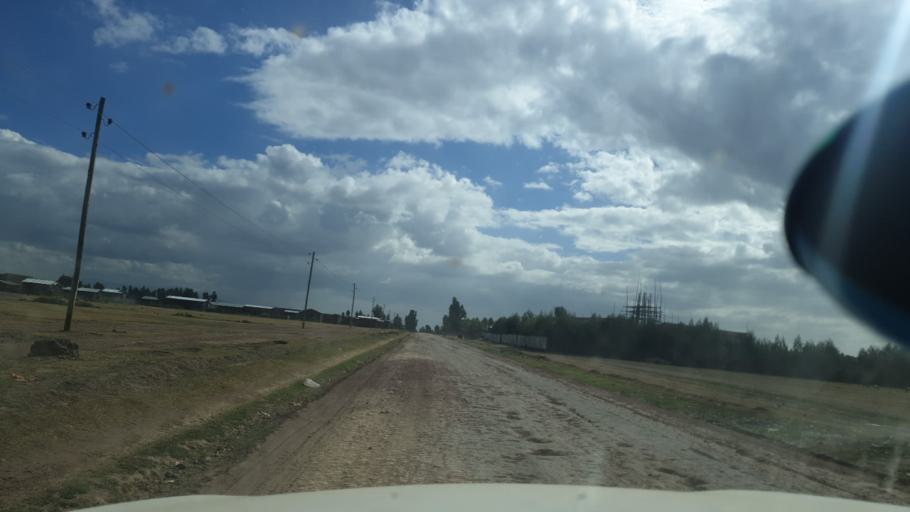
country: ET
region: Oromiya
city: Ziway
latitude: 7.7284
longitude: 39.0304
